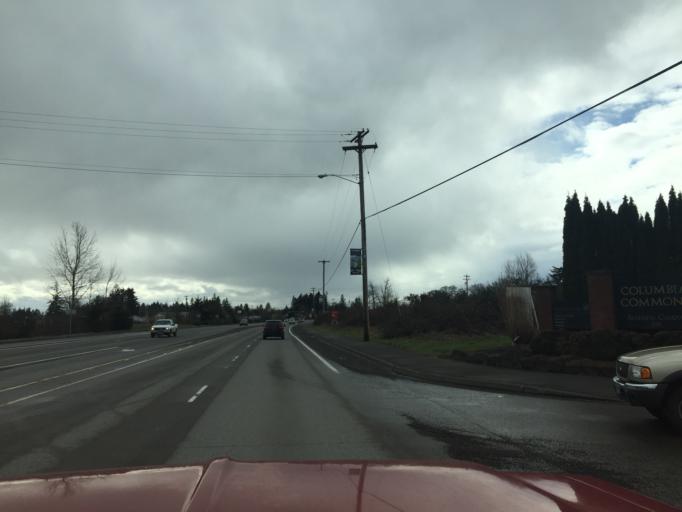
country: US
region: Oregon
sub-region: Columbia County
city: Saint Helens
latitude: 45.8639
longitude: -122.8181
